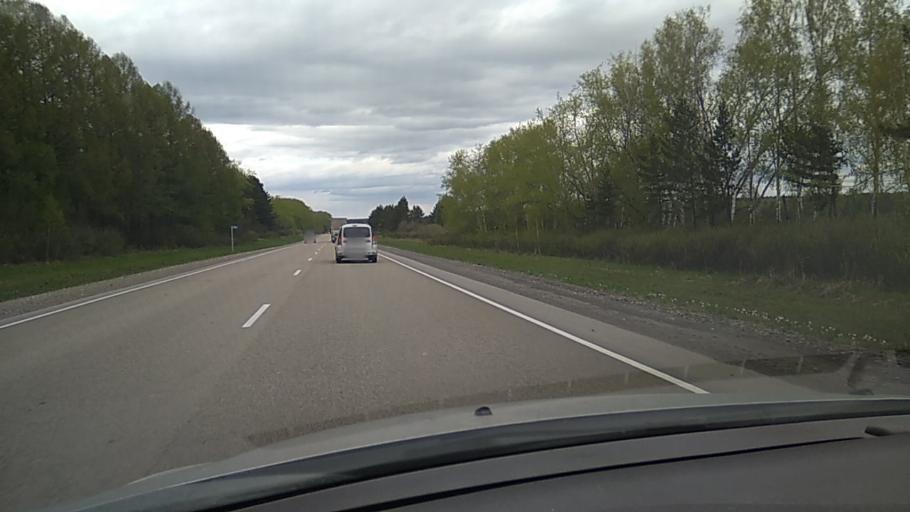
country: RU
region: Sverdlovsk
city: Dvurechensk
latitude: 56.6684
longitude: 61.1528
